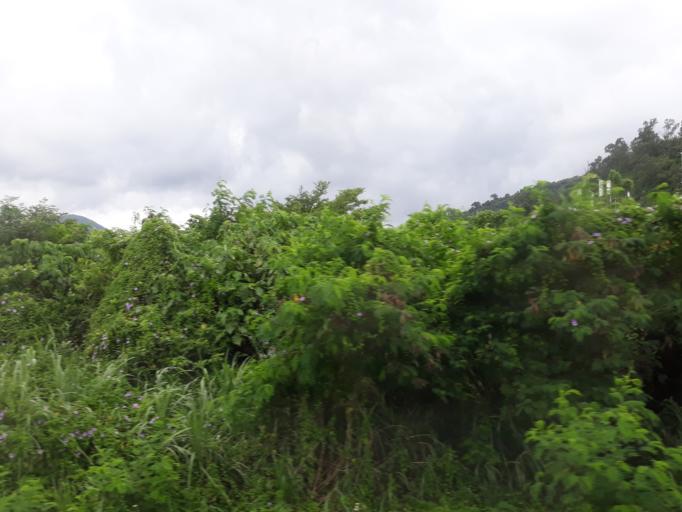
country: TW
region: Taiwan
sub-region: Yilan
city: Yilan
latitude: 24.6155
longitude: 121.8130
